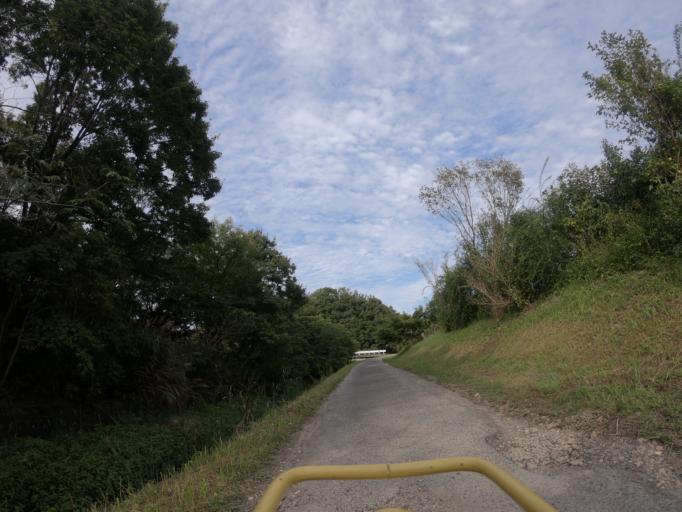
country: JP
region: Aichi
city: Seto
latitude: 35.1473
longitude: 137.0885
